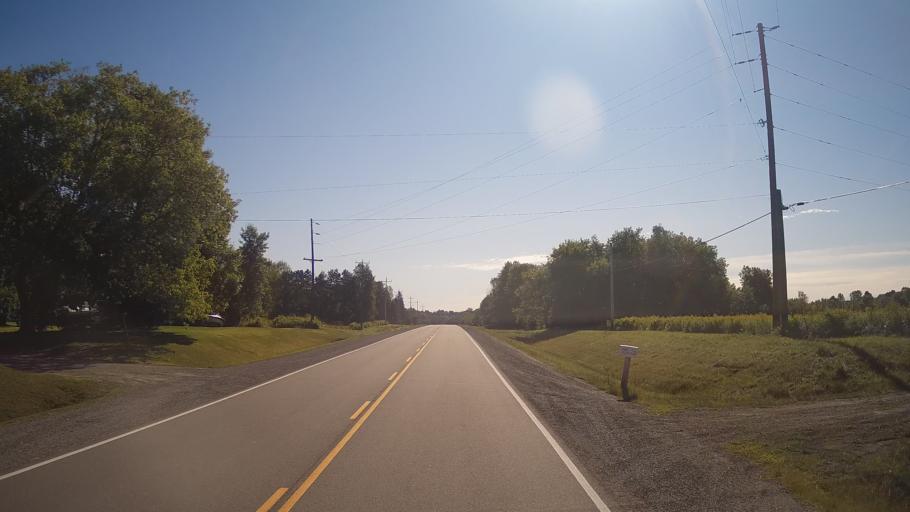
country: CA
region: Ontario
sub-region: Lanark County
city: Smiths Falls
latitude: 44.6263
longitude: -76.0036
